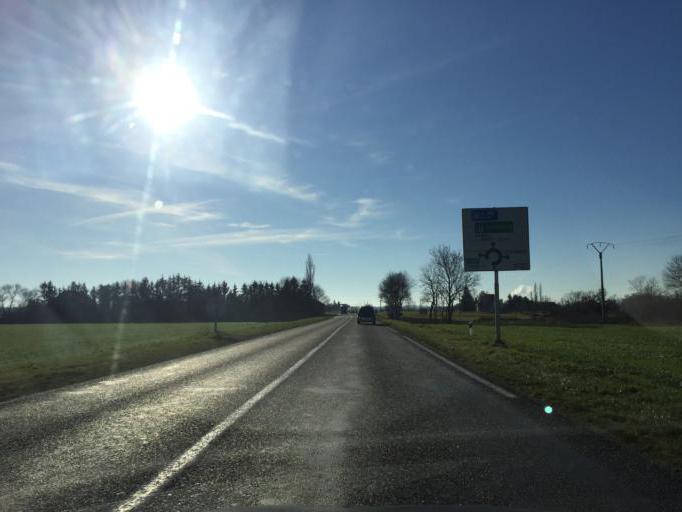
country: FR
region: Auvergne
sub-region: Departement de l'Allier
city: Saint-Pourcain-sur-Sioule
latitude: 46.2679
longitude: 3.2897
